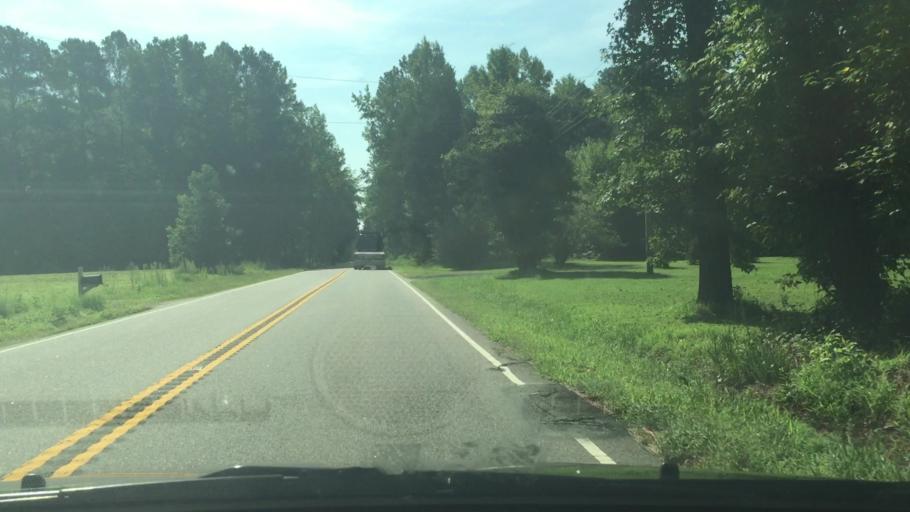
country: US
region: Virginia
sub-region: Sussex County
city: Sussex
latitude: 37.0223
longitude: -77.2882
